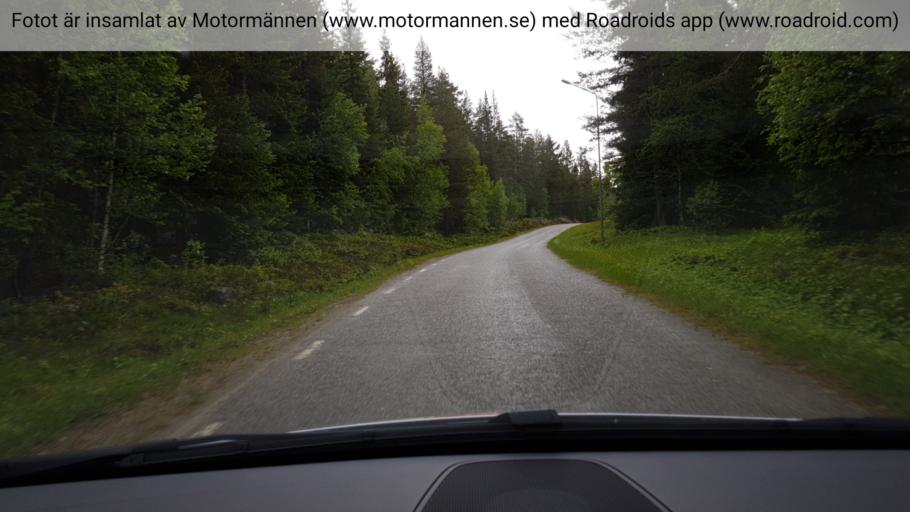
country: SE
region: Jaemtland
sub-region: Harjedalens Kommun
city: Sveg
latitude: 62.2411
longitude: 13.3449
